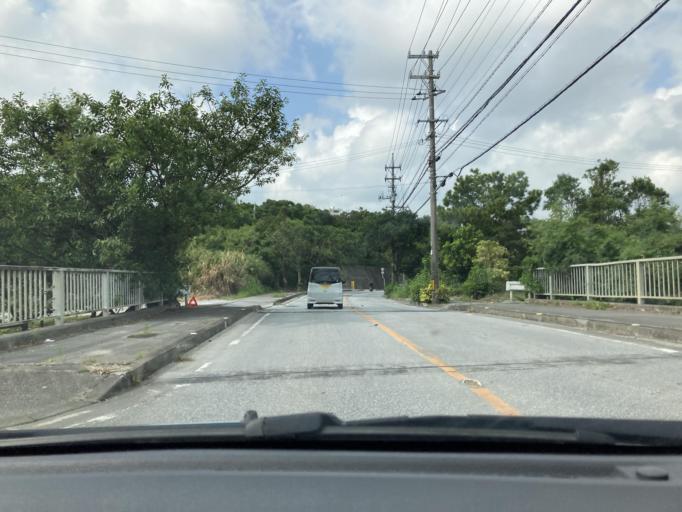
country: JP
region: Okinawa
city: Ginowan
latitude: 26.2737
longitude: 127.7812
